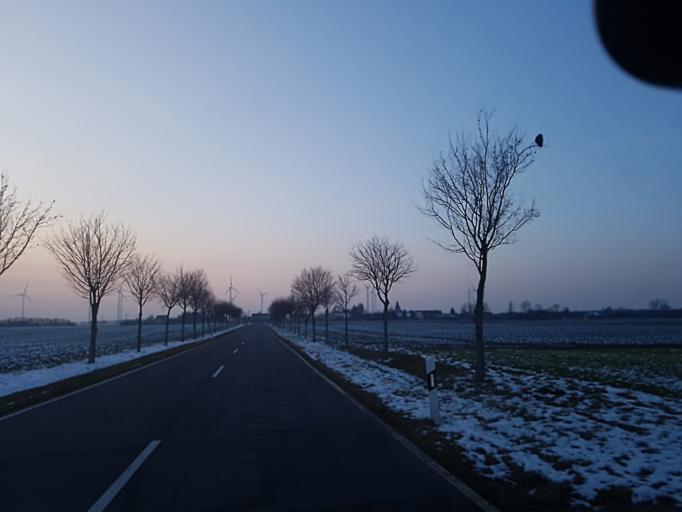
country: DE
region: Brandenburg
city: Muhlberg
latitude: 51.4708
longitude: 13.2772
